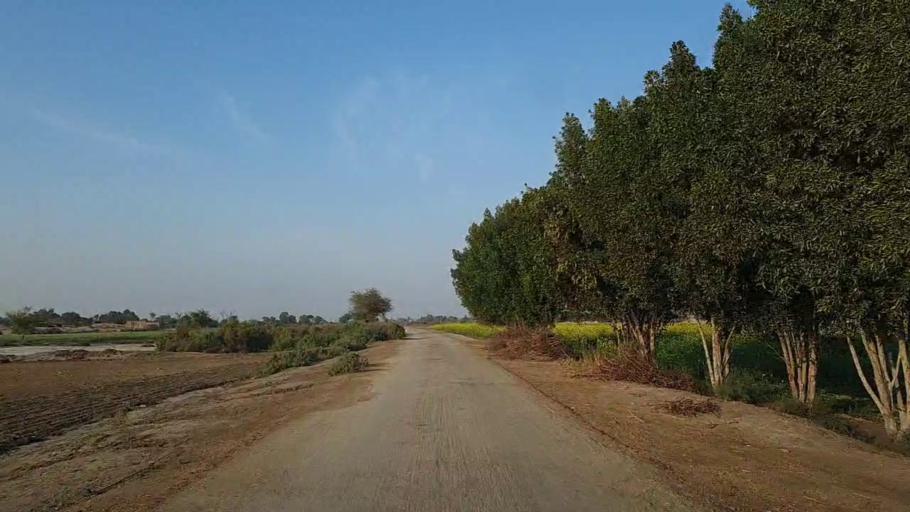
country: PK
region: Sindh
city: Jam Sahib
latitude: 26.3714
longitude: 68.5372
